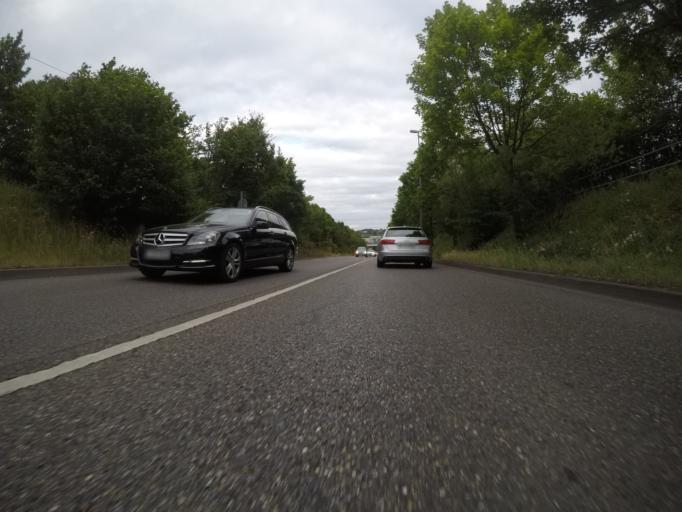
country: DE
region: Baden-Wuerttemberg
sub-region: Regierungsbezirk Stuttgart
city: Stuttgart Feuerbach
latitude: 48.8115
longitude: 9.1380
